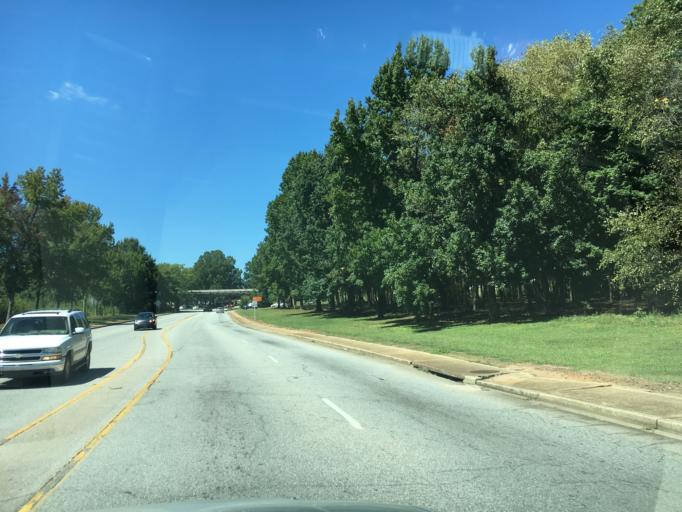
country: US
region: South Carolina
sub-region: Greenville County
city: Dunean
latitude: 34.8175
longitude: -82.4166
